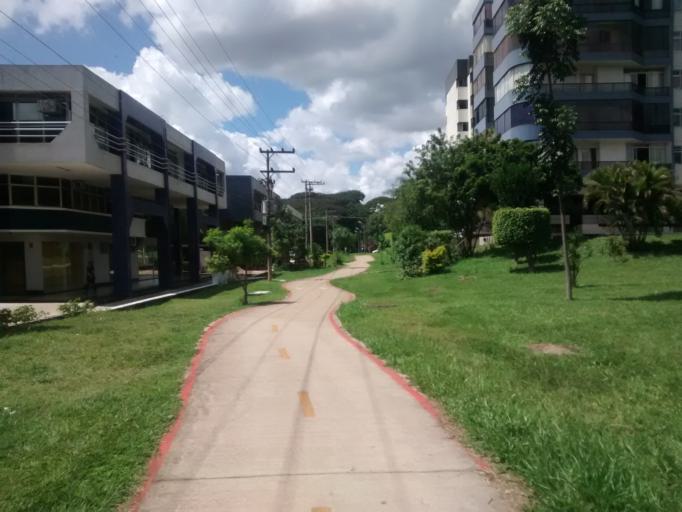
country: BR
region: Federal District
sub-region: Brasilia
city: Brasilia
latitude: -15.7519
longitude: -47.8855
